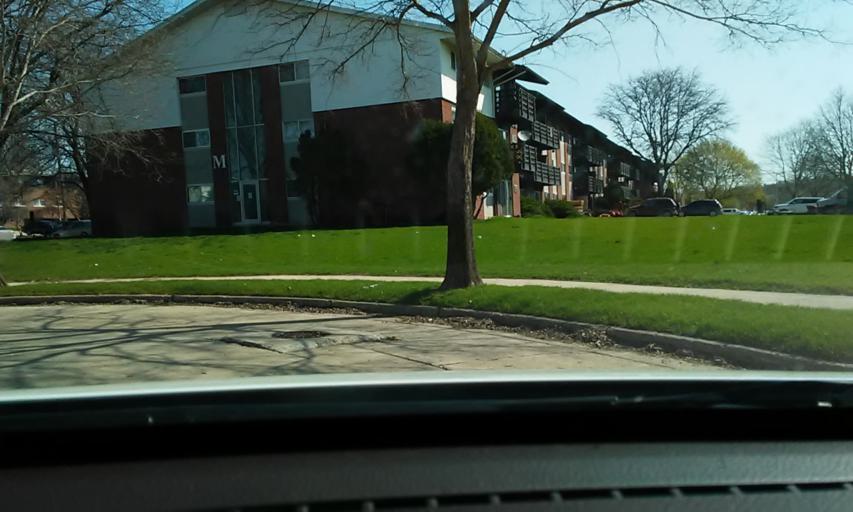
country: US
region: Wisconsin
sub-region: Milwaukee County
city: Greenfield
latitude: 42.9815
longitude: -88.0494
